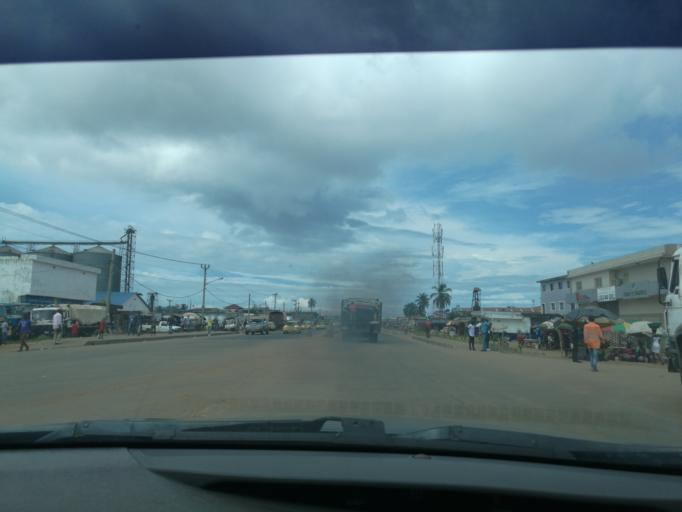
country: LR
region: Montserrado
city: Monrovia
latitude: 6.3387
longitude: -10.7880
